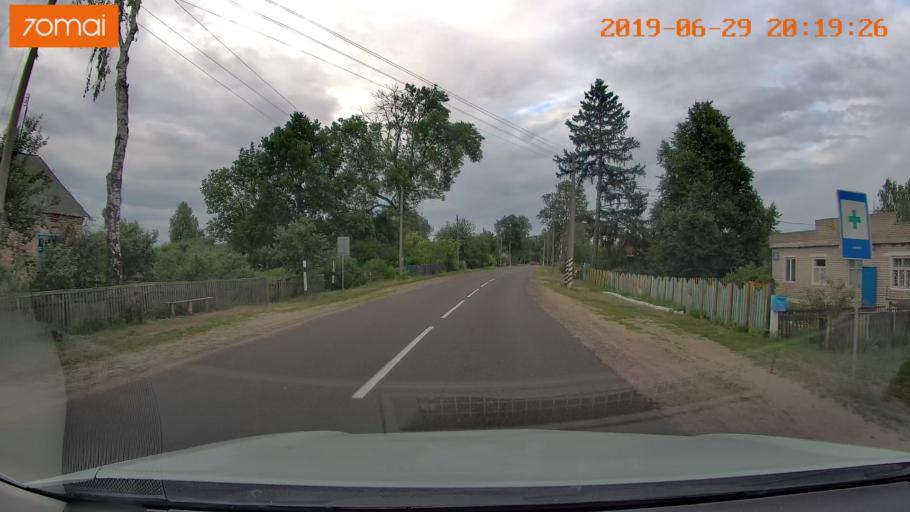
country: BY
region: Brest
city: Asnyezhytsy
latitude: 52.4012
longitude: 26.2442
